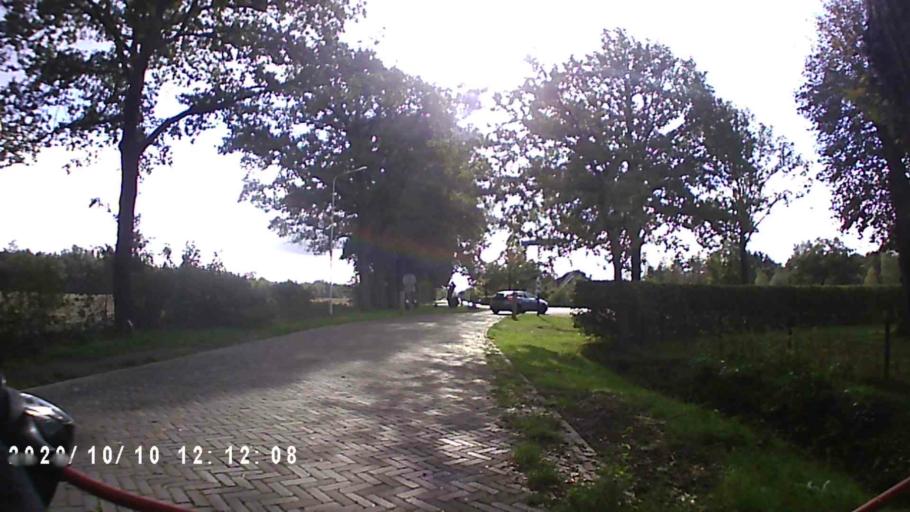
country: NL
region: Friesland
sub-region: Gemeente Heerenveen
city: Jubbega
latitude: 53.0374
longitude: 6.1523
